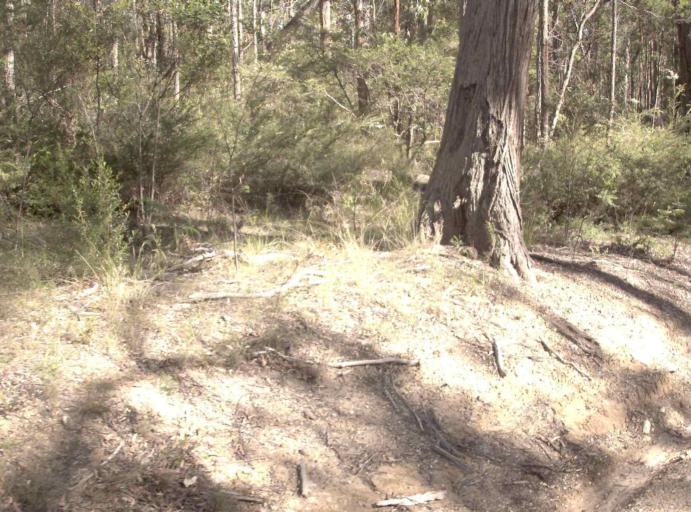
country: AU
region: Victoria
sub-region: East Gippsland
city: Lakes Entrance
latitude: -37.6780
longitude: 148.0545
